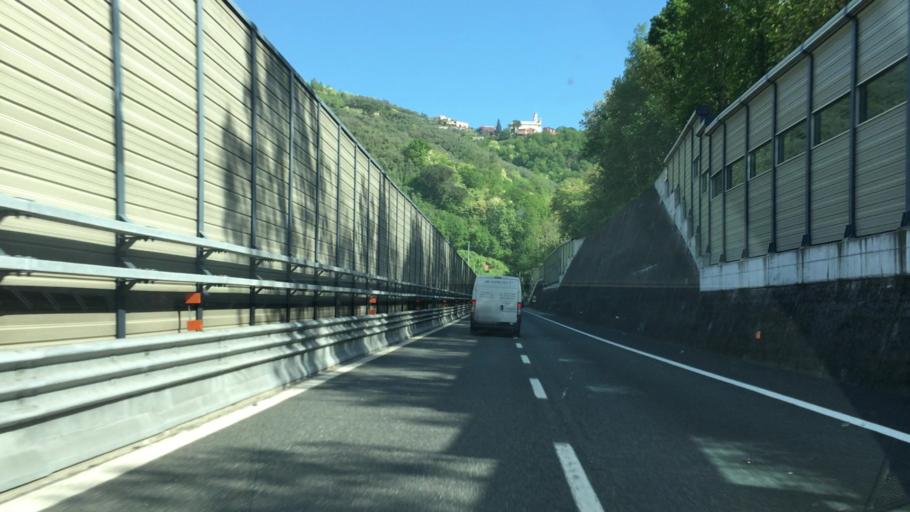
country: IT
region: Liguria
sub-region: Provincia di Genova
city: Lavagna
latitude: 44.3080
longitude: 9.3650
